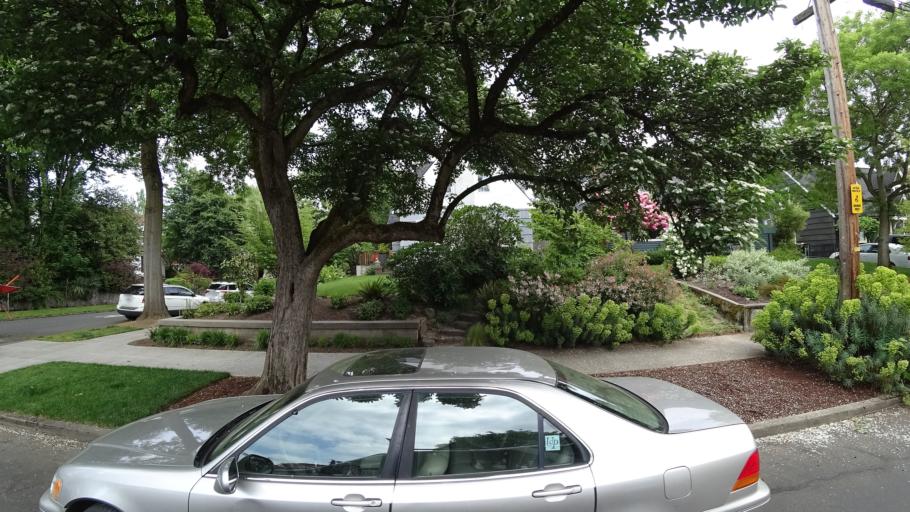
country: US
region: Oregon
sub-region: Multnomah County
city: Portland
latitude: 45.5450
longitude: -122.6525
